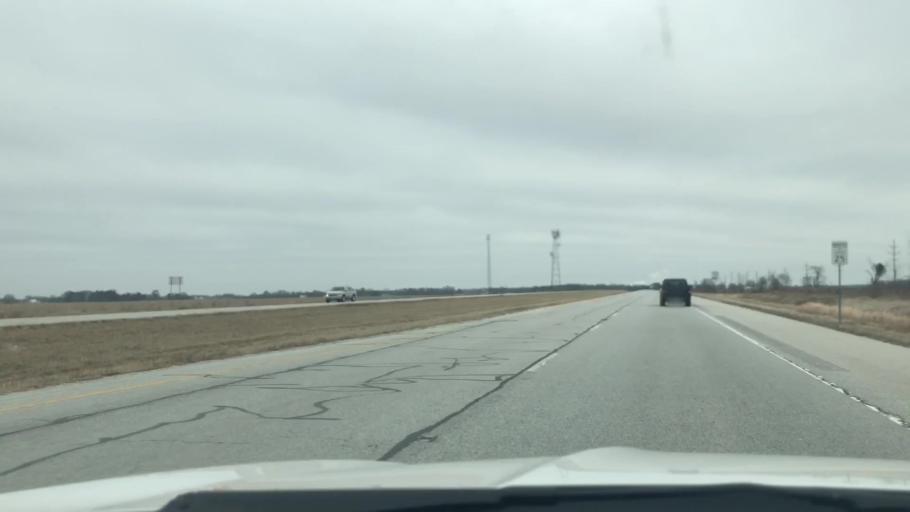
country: US
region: Indiana
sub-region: Cass County
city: Georgetown
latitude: 40.6635
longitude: -86.5334
